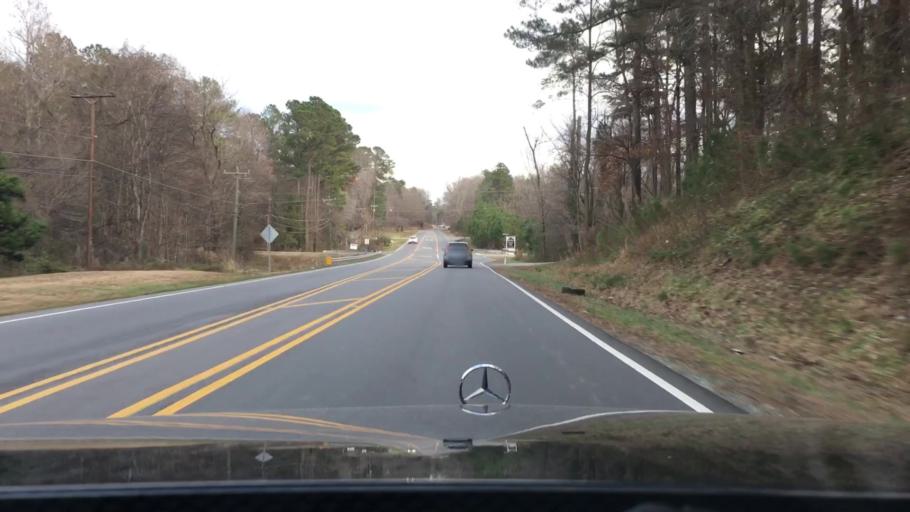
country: US
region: North Carolina
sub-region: Orange County
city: Hillsborough
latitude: 36.0849
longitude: -79.0908
